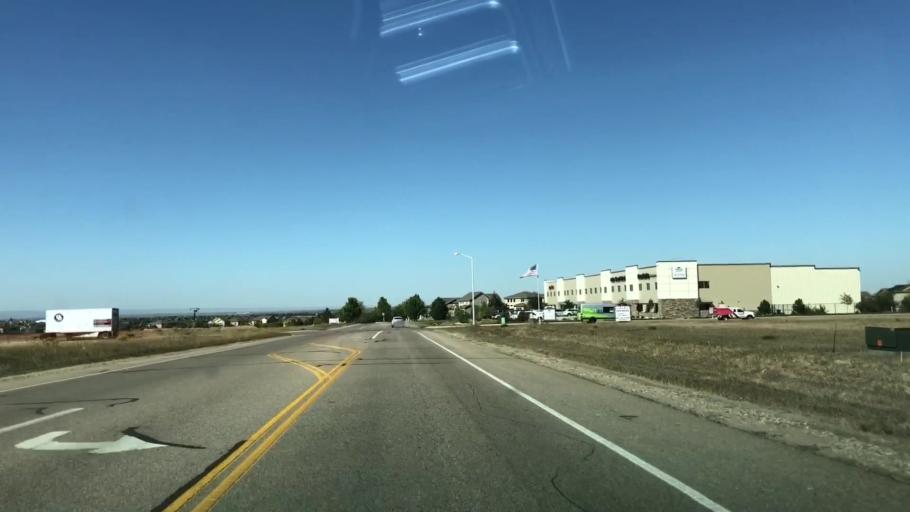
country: US
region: Colorado
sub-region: Weld County
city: Windsor
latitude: 40.4379
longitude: -104.9676
